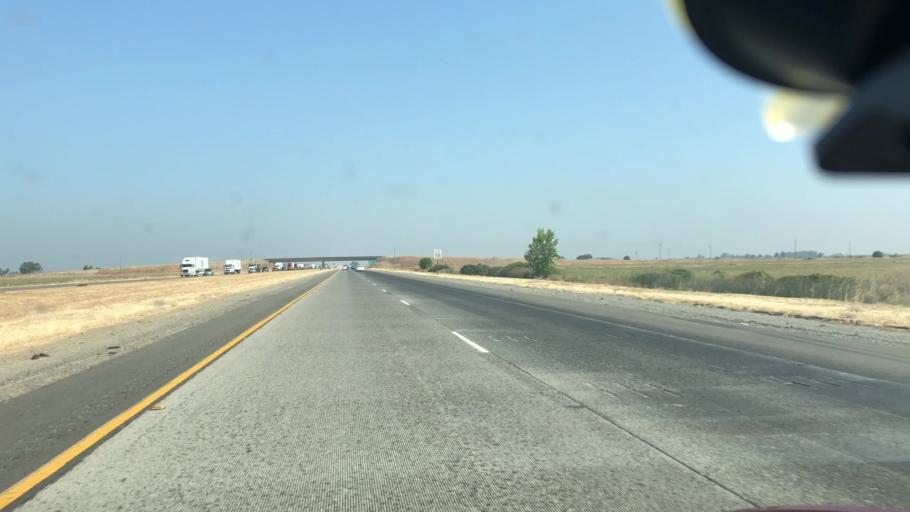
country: US
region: California
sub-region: Sacramento County
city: Walnut Grove
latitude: 38.2939
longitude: -121.4597
